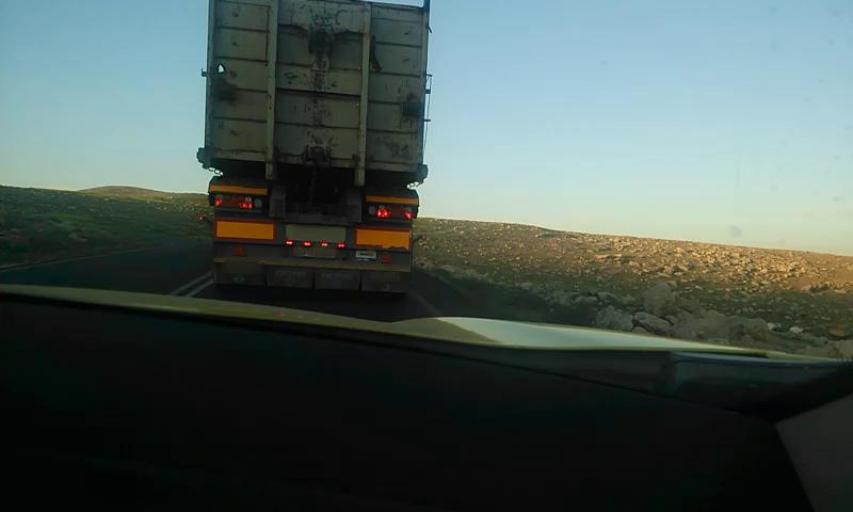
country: PS
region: West Bank
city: Rammun
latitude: 31.9167
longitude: 35.3463
